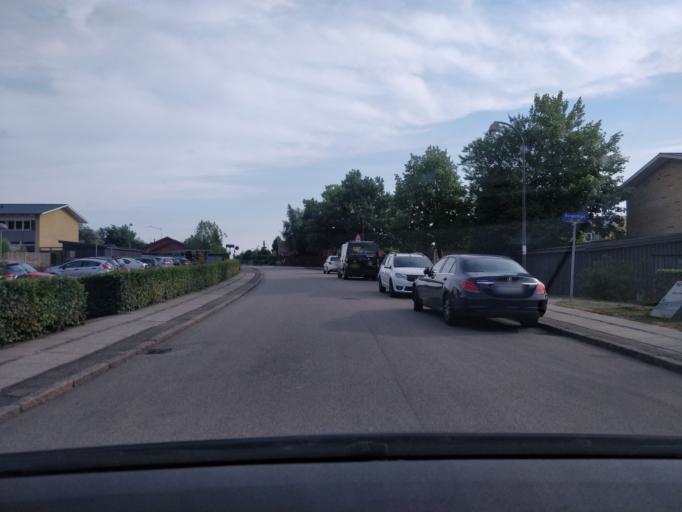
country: DK
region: Capital Region
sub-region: Herlev Kommune
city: Herlev
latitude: 55.7302
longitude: 12.4231
